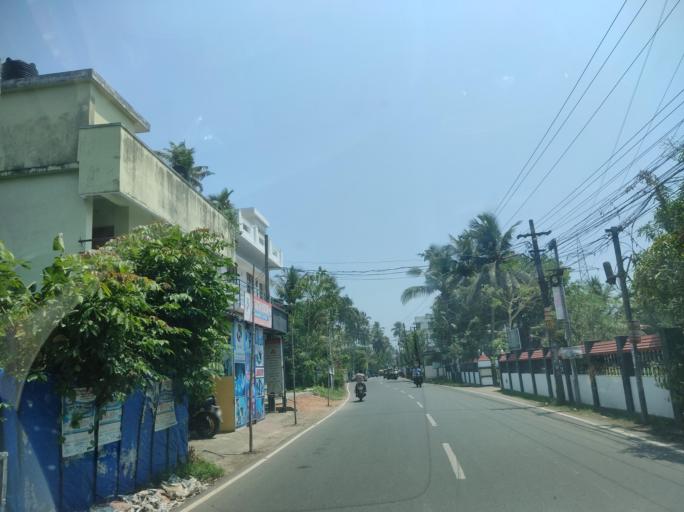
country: IN
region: Kerala
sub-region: Ernakulam
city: Cochin
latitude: 9.8961
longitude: 76.2842
